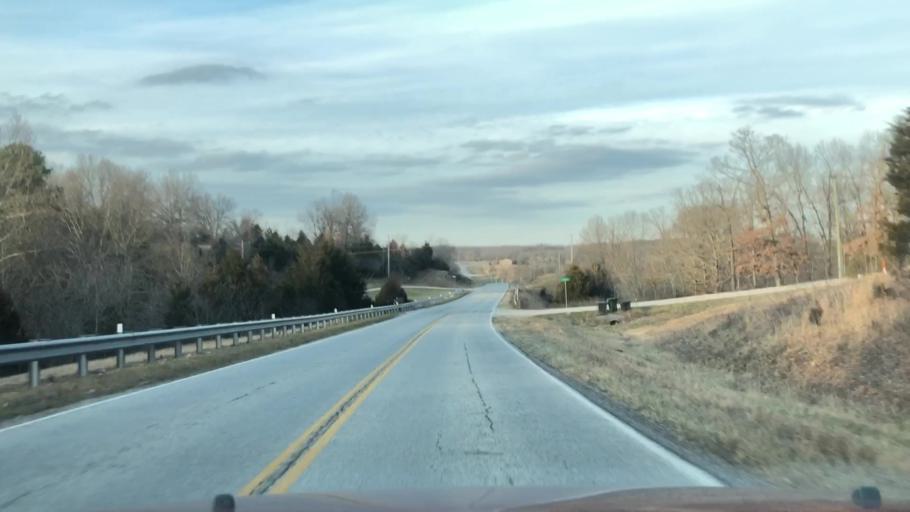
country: US
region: Missouri
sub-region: Webster County
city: Marshfield
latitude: 37.2401
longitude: -92.8800
